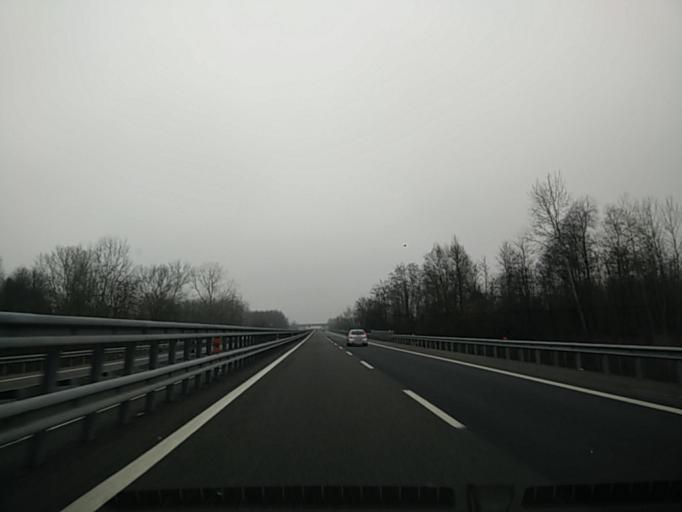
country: IT
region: Piedmont
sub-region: Provincia di Asti
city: Villafranca d'Asti
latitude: 44.9262
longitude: 8.0131
